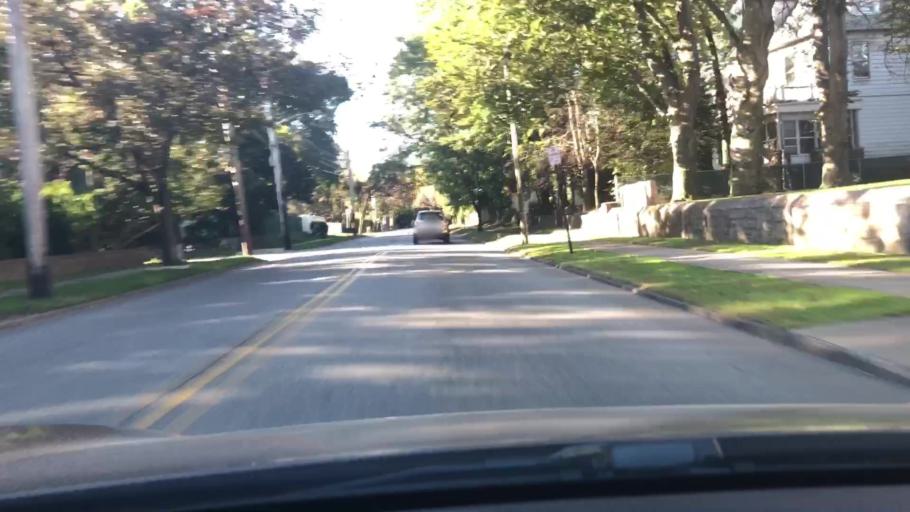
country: US
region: New York
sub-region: Westchester County
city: Mount Vernon
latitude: 40.9218
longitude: -73.8237
